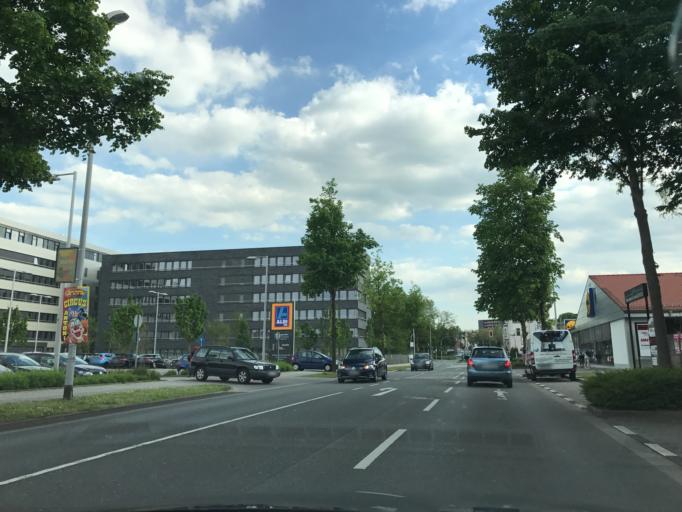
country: DE
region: North Rhine-Westphalia
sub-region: Regierungsbezirk Dusseldorf
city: Muelheim (Ruhr)
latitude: 51.4116
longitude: 6.8686
